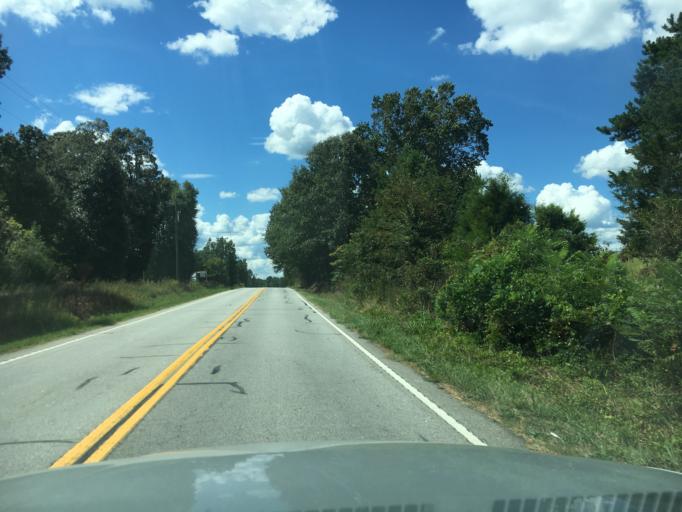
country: US
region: South Carolina
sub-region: Greenwood County
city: Ware Shoals
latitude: 34.5199
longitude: -82.1698
